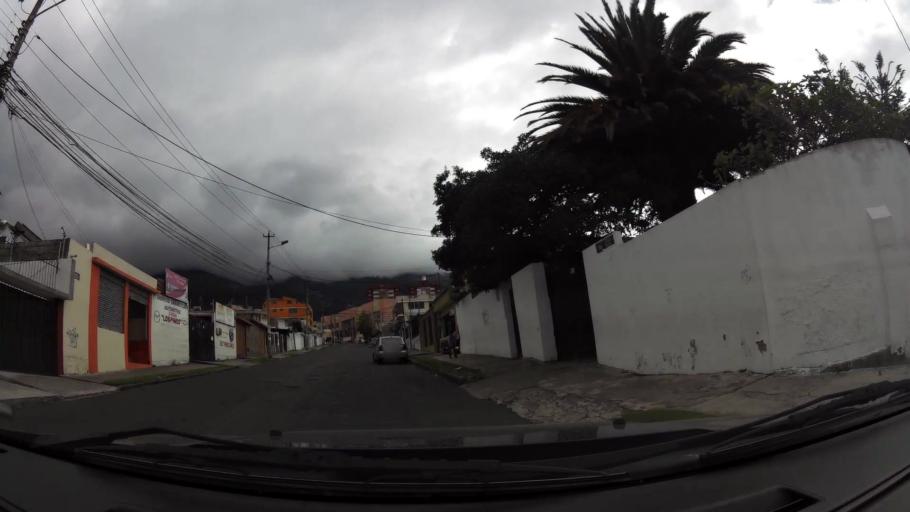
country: EC
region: Pichincha
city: Quito
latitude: -0.1397
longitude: -78.4987
